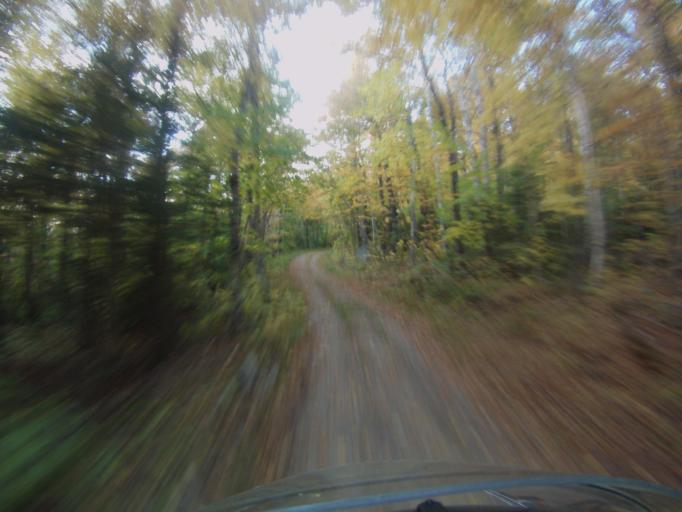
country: US
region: Vermont
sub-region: Addison County
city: Bristol
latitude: 44.0998
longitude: -72.9536
